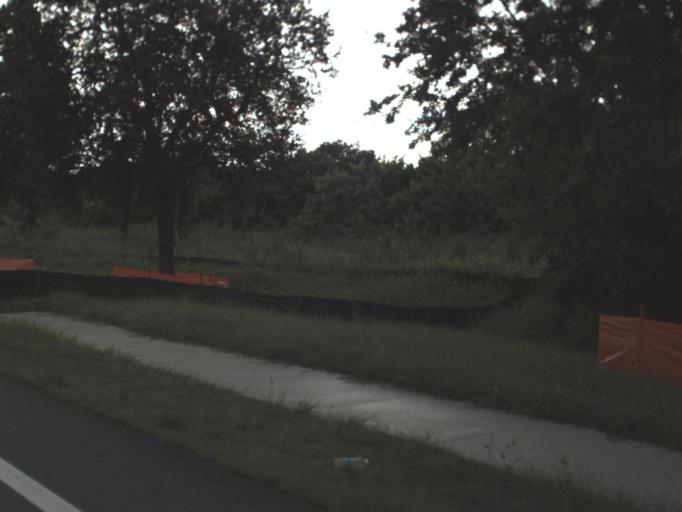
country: US
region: Florida
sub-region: Sarasota County
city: Lake Sarasota
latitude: 27.2987
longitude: -82.4423
